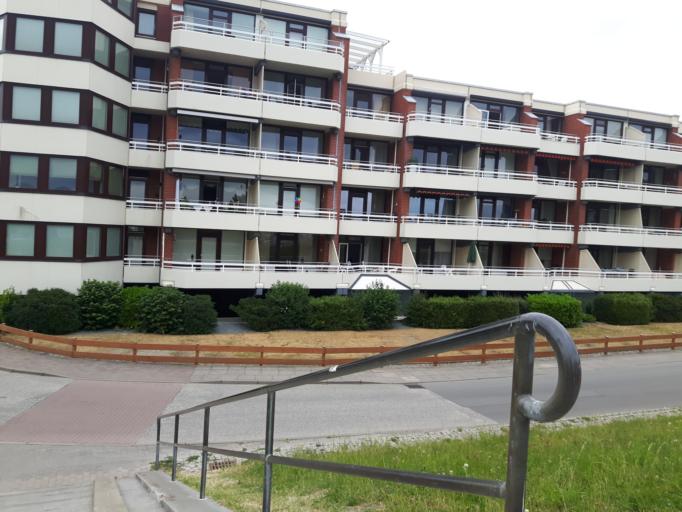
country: DE
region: Schleswig-Holstein
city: Gromitz
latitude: 54.1479
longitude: 10.9700
